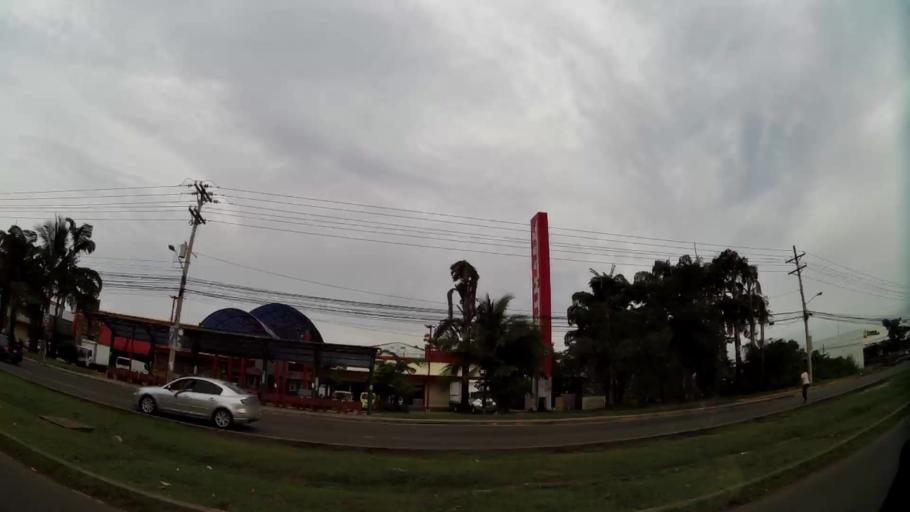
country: PA
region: Panama
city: San Miguelito
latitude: 9.0448
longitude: -79.4525
